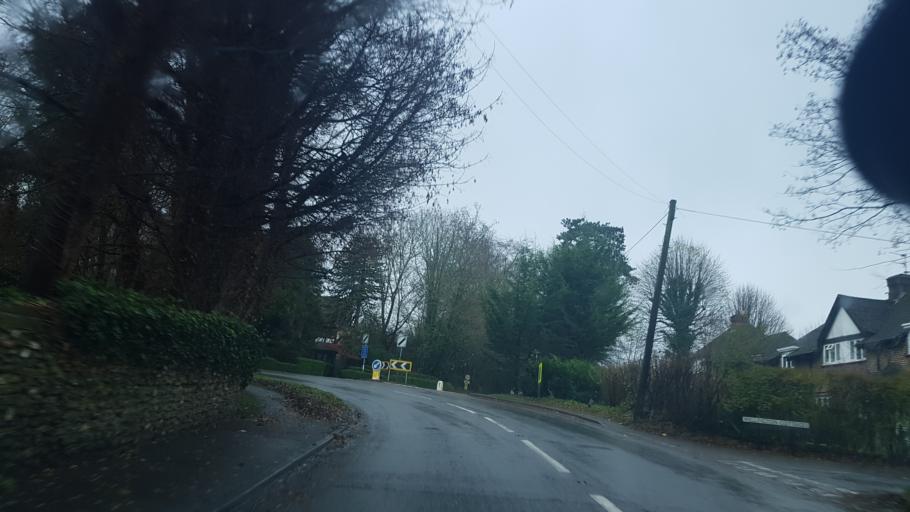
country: GB
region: England
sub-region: Surrey
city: East Horsley
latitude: 51.2614
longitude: -0.4312
